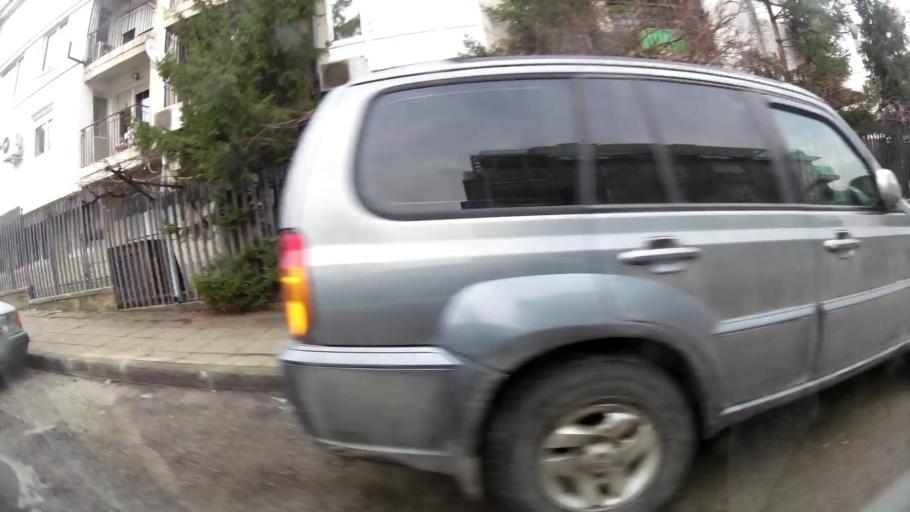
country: BG
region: Sofia-Capital
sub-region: Stolichna Obshtina
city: Sofia
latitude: 42.6686
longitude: 23.2454
